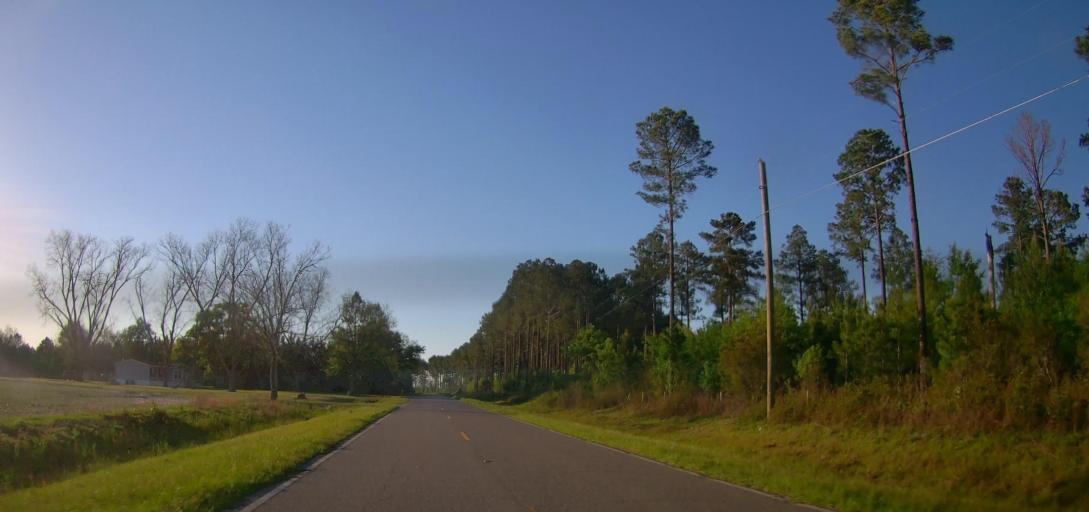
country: US
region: Georgia
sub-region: Ben Hill County
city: Fitzgerald
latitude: 31.6754
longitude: -83.2158
